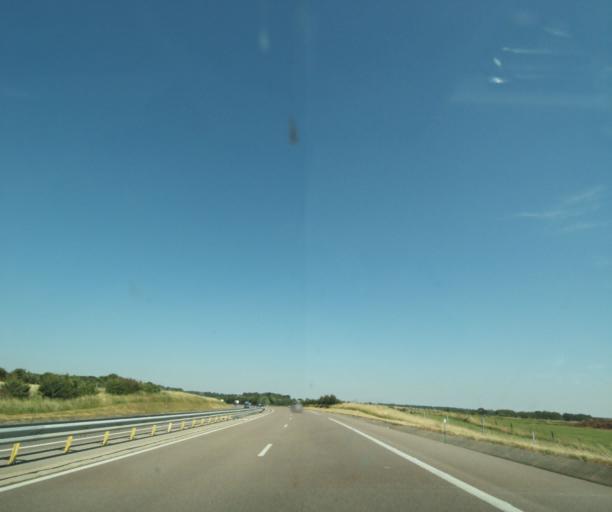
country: FR
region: Lorraine
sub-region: Departement des Vosges
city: Chatenois
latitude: 48.4038
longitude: 5.8785
